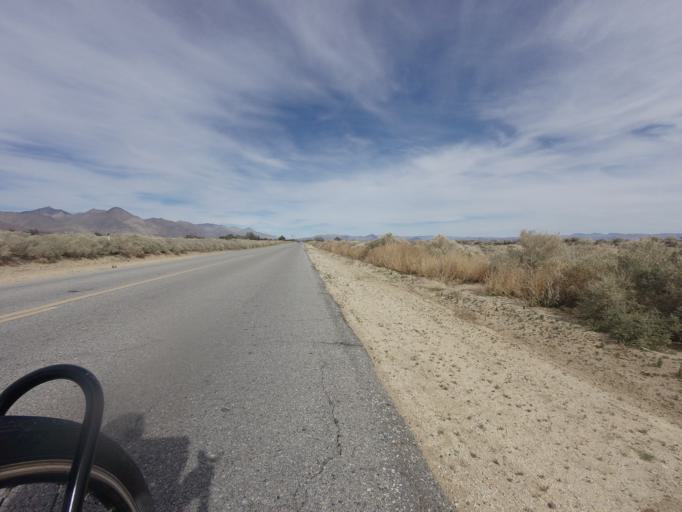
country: US
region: California
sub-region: Kern County
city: Inyokern
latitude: 35.7212
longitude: -117.8344
